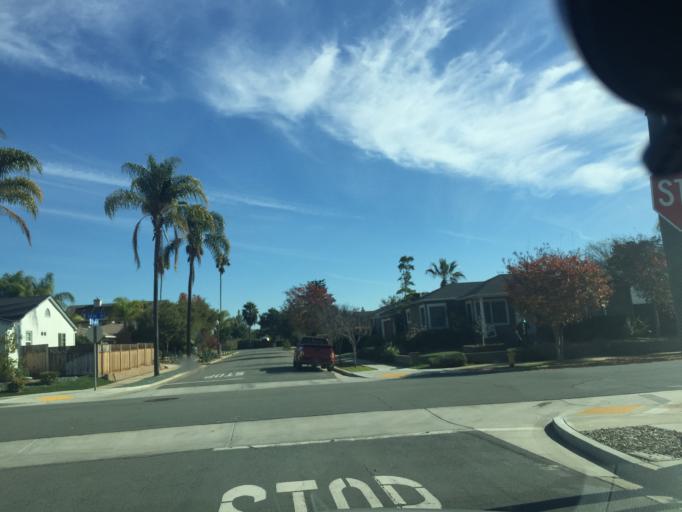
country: US
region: California
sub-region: San Diego County
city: Lemon Grove
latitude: 32.7651
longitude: -117.0870
